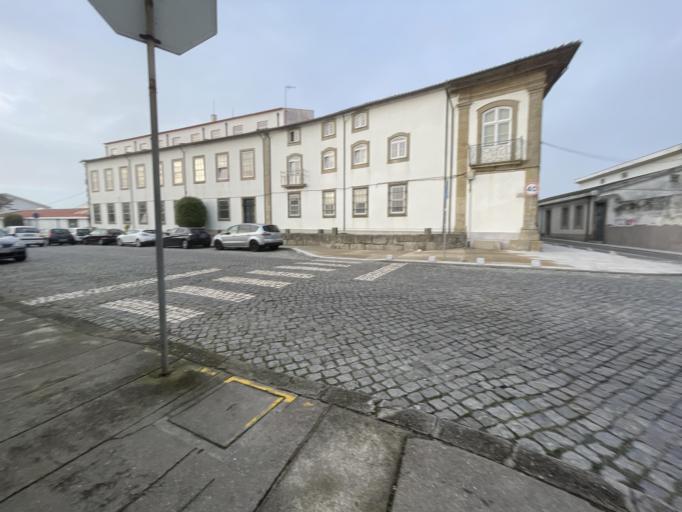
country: PT
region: Porto
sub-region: Vila do Conde
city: Vila do Conde
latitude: 41.3557
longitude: -8.7441
